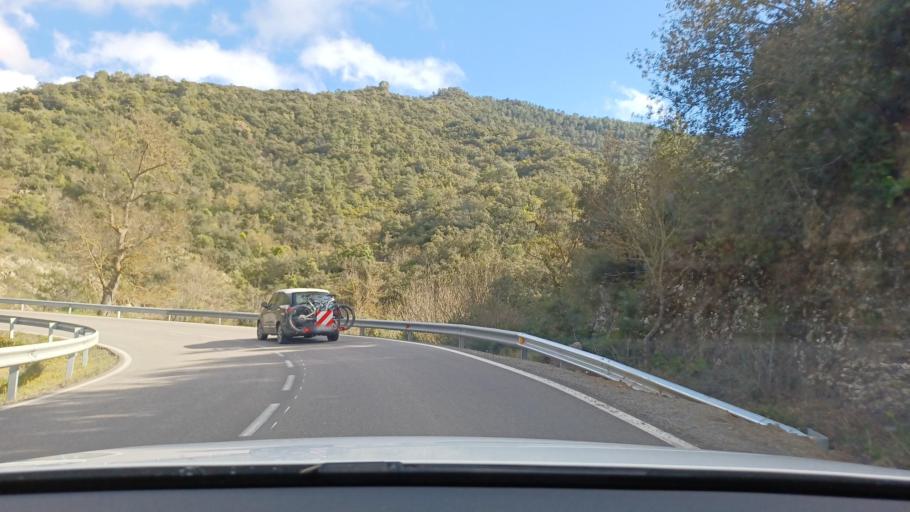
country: ES
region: Catalonia
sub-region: Provincia de Tarragona
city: Alforja
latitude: 41.2244
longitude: 0.9078
